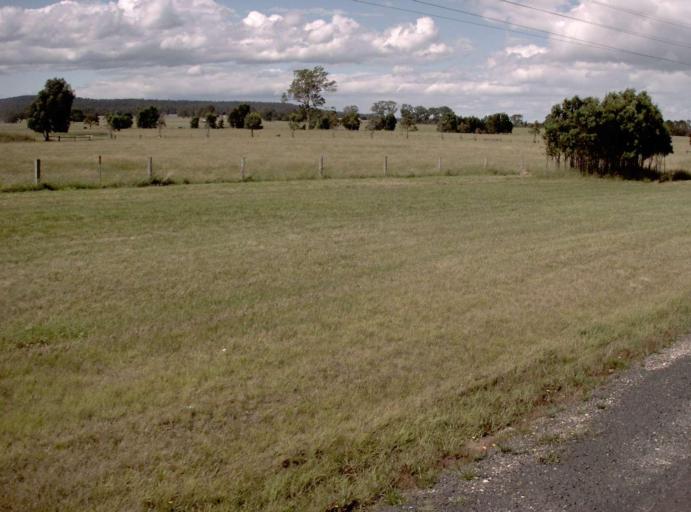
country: AU
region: Victoria
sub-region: Latrobe
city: Traralgon
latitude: -38.1394
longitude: 146.5333
